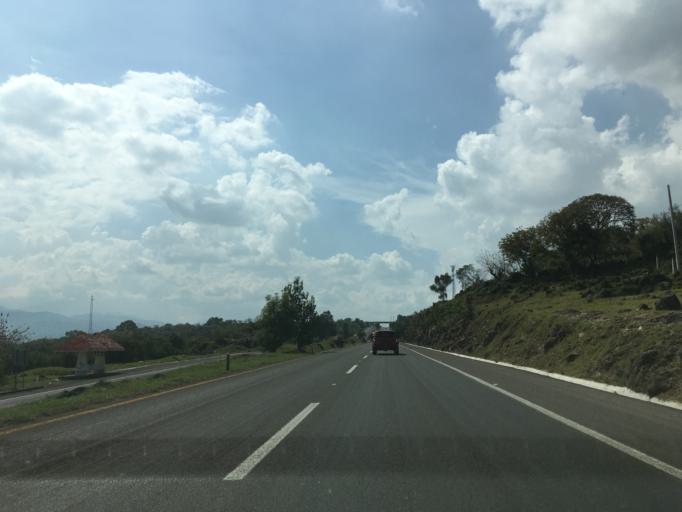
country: MX
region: Michoacan
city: Acuitzio del Canje
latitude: 19.5550
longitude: -101.3452
